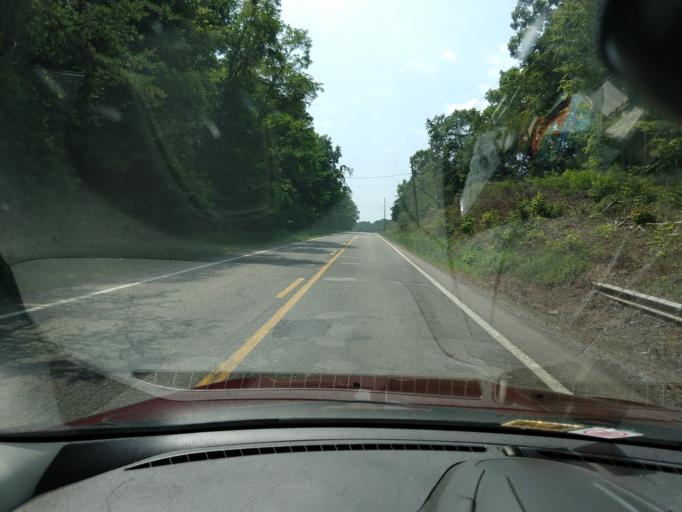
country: US
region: West Virginia
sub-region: Jackson County
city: Ripley
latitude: 38.8484
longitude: -81.7991
